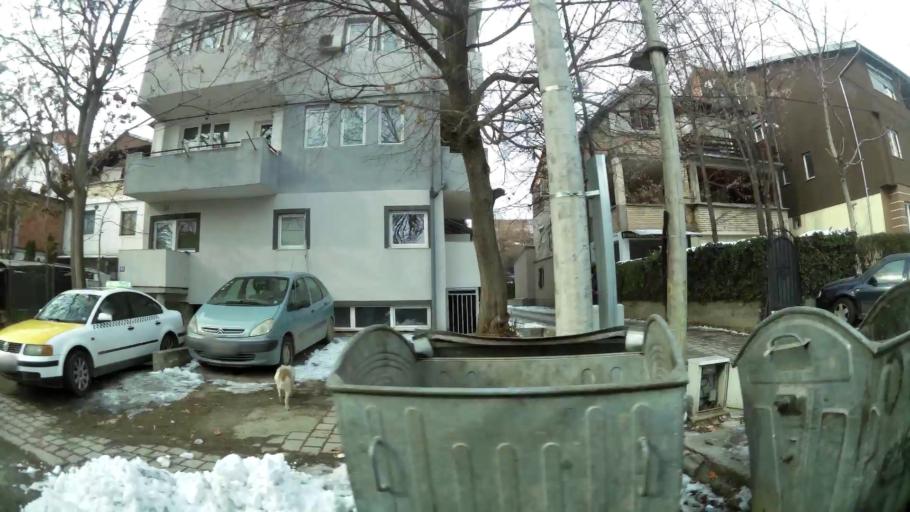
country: MK
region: Cair
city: Cair
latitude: 42.0118
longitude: 21.4431
